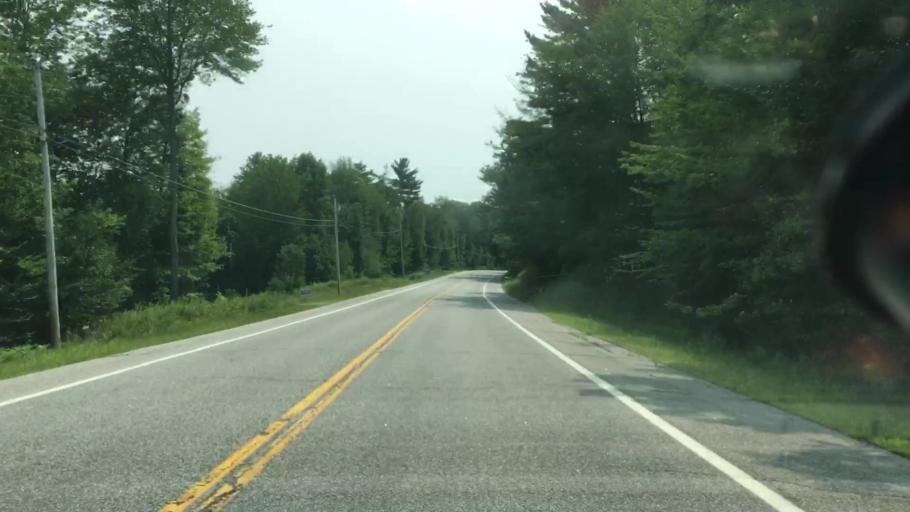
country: US
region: Maine
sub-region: Kennebec County
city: Wayne
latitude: 44.3709
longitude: -70.0934
